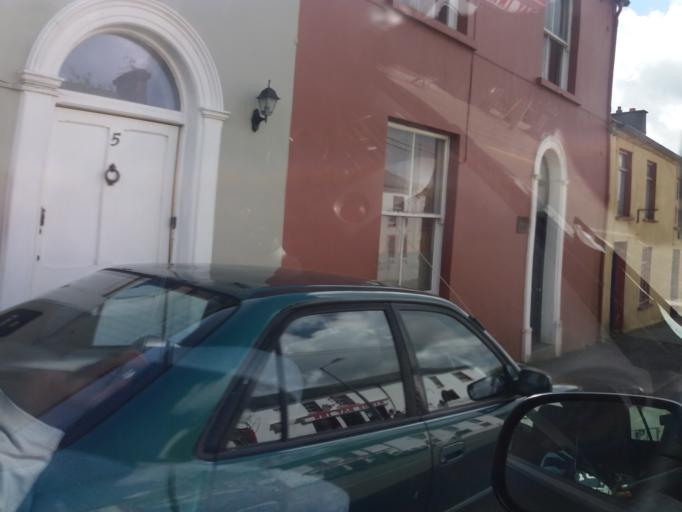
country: IE
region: Munster
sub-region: Waterford
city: Dunmore East
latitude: 52.2420
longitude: -6.9513
